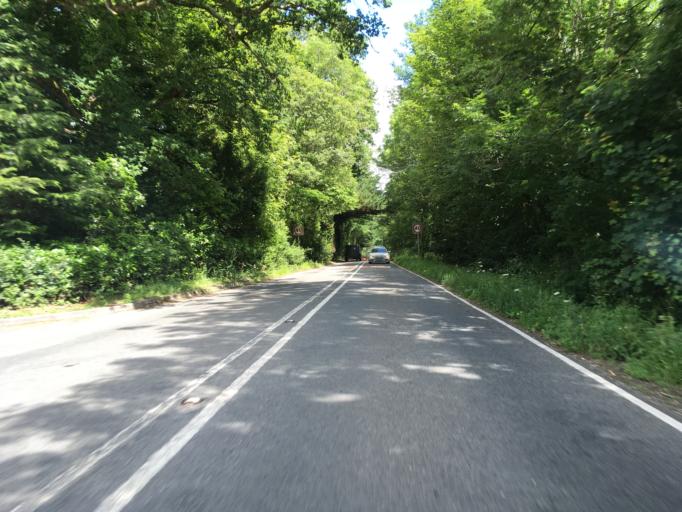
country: GB
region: England
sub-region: Hampshire
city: Highclere
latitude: 51.3457
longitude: -1.3715
